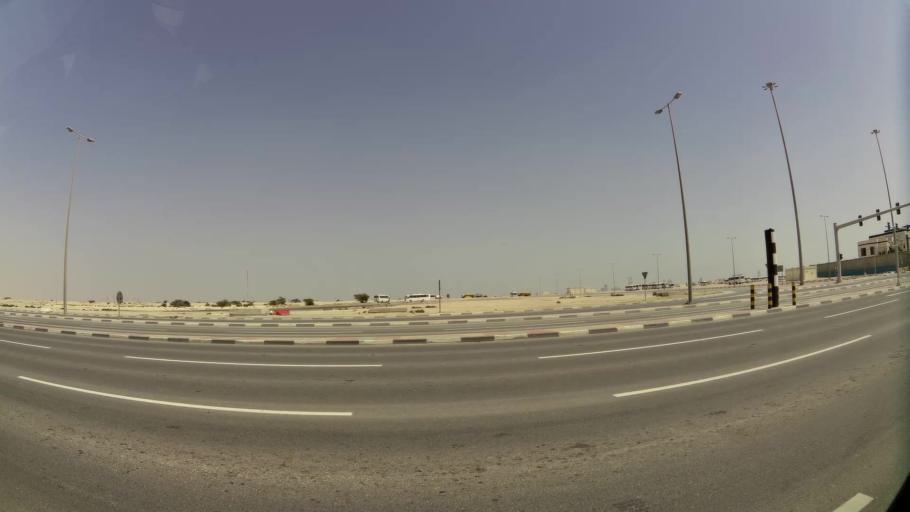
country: QA
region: Baladiyat Umm Salal
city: Umm Salal Muhammad
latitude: 25.3906
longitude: 51.4646
